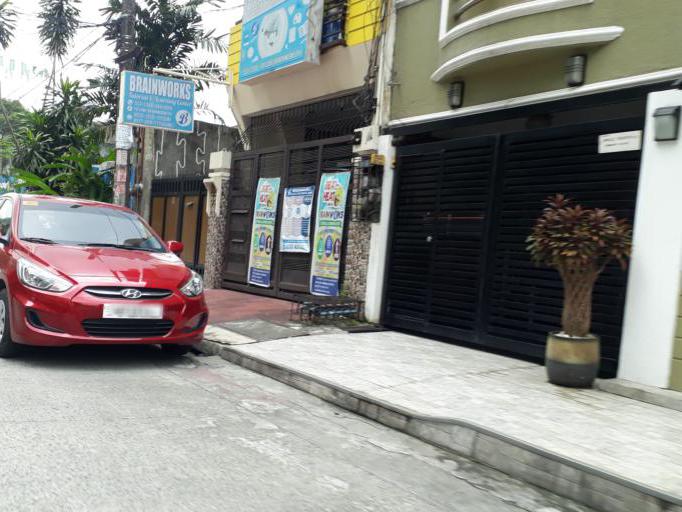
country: PH
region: Calabarzon
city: Bagong Pagasa
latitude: 14.6564
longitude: 121.0340
